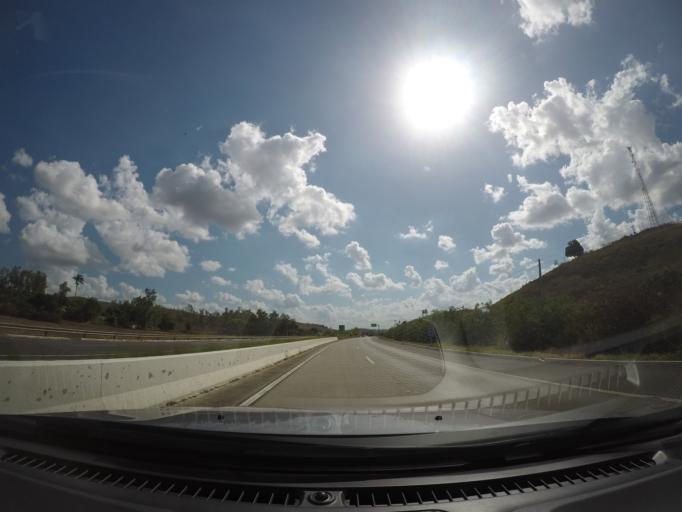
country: BR
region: Pernambuco
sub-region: Ribeirao
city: Ribeirao
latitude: -8.4302
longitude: -35.3243
